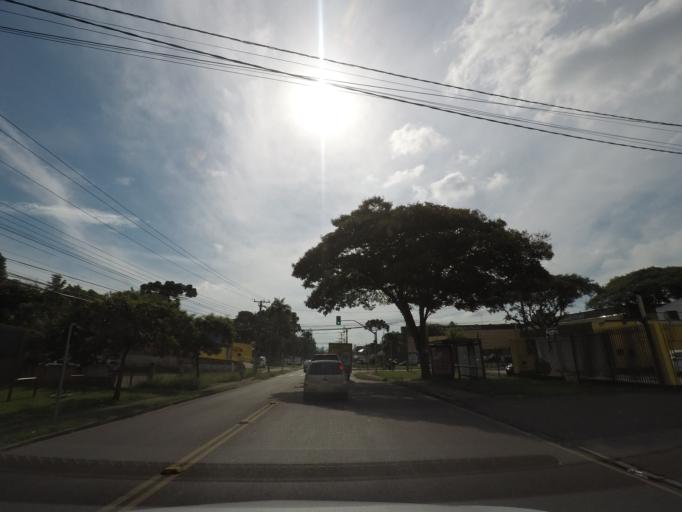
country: BR
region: Parana
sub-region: Curitiba
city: Curitiba
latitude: -25.4641
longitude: -49.2451
